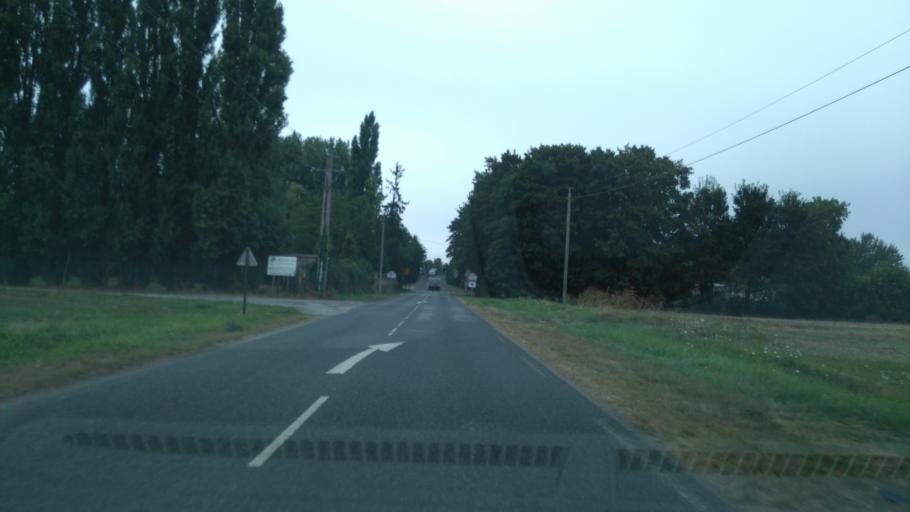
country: FR
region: Picardie
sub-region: Departement de l'Oise
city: Precy-sur-Oise
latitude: 49.2006
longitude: 2.3774
